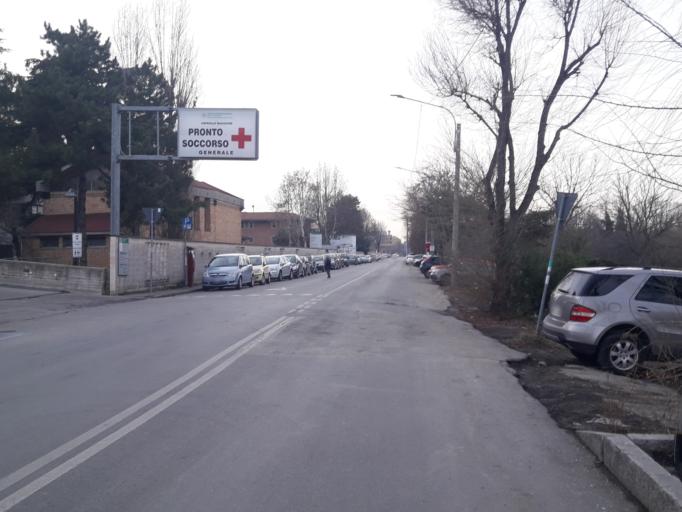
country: IT
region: Emilia-Romagna
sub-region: Provincia di Bologna
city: Bologna
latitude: 44.5065
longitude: 11.3160
